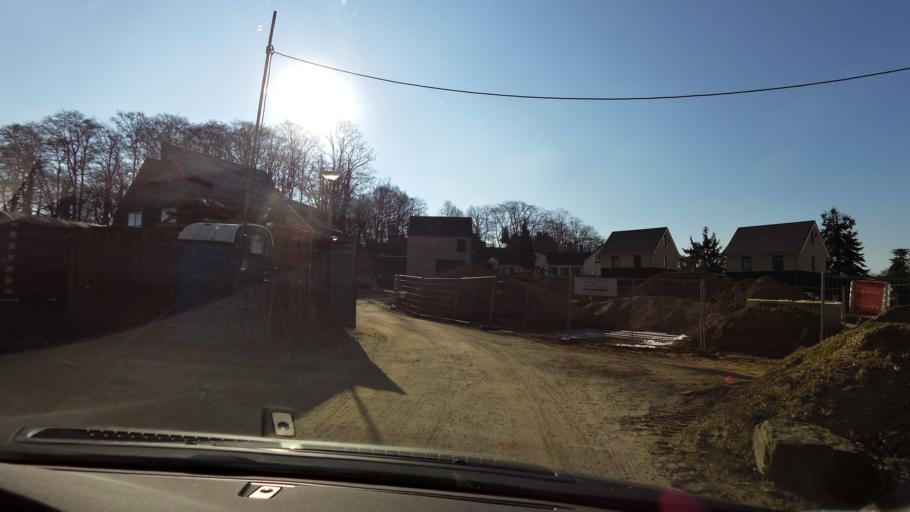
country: NL
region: Limburg
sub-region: Gemeente Schinnen
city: Amstenrade
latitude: 50.9307
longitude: 5.9095
